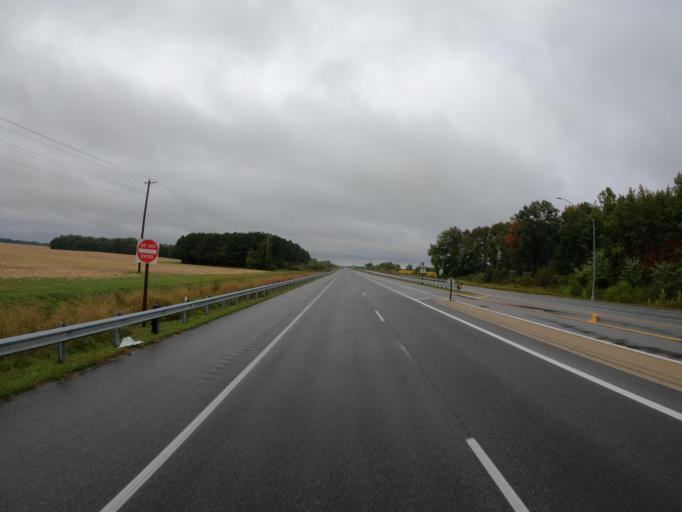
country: US
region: Maryland
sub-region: Queen Anne's County
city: Centreville
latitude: 38.9312
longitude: -76.0216
